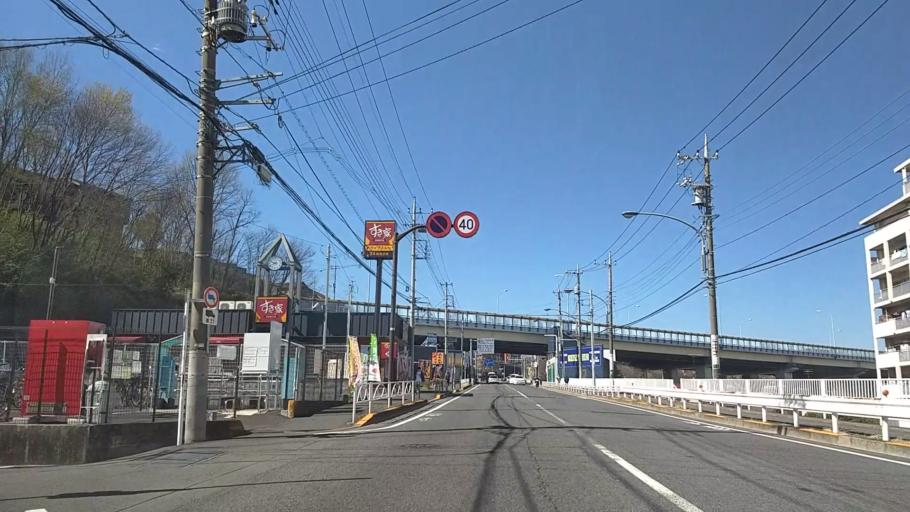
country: JP
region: Tokyo
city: Hino
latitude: 35.6790
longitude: 139.3910
